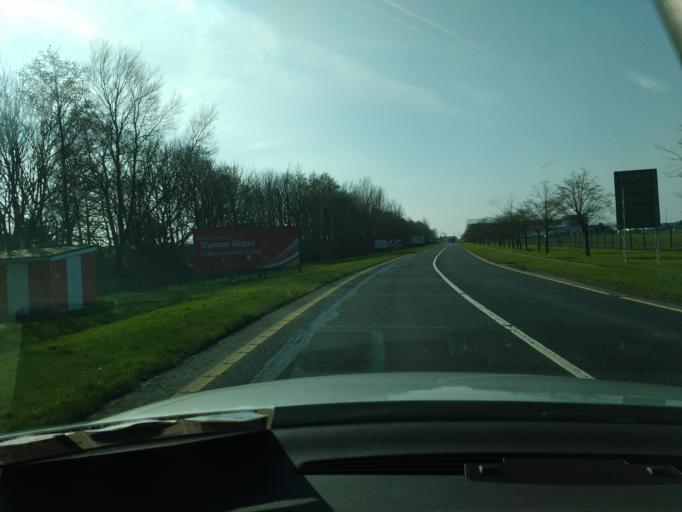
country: IE
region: Munster
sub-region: An Clar
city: Shannon
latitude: 52.6918
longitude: -8.9046
